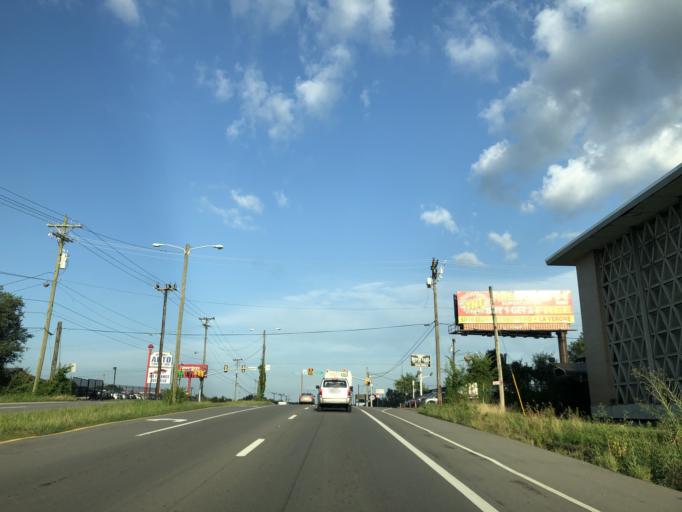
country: US
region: Tennessee
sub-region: Davidson County
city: Nashville
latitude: 36.1394
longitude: -86.7343
